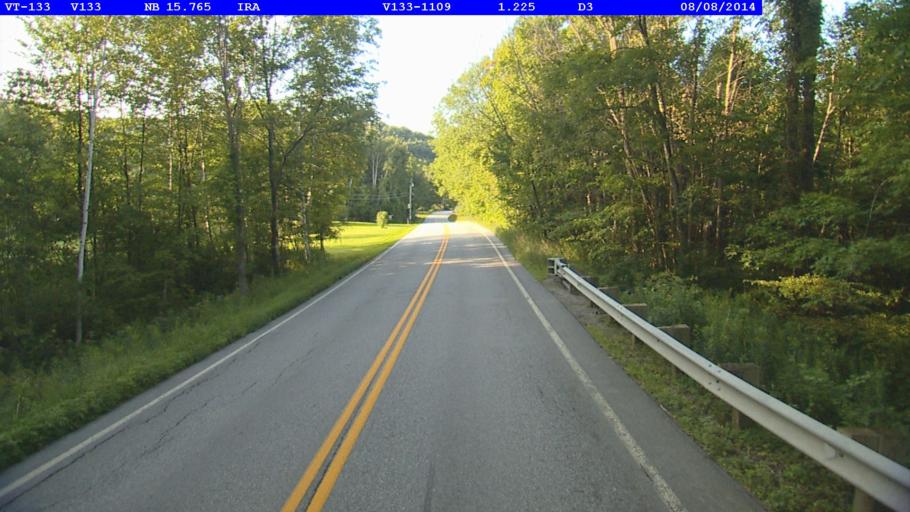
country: US
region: Vermont
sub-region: Rutland County
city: West Rutland
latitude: 43.5117
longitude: -73.0734
